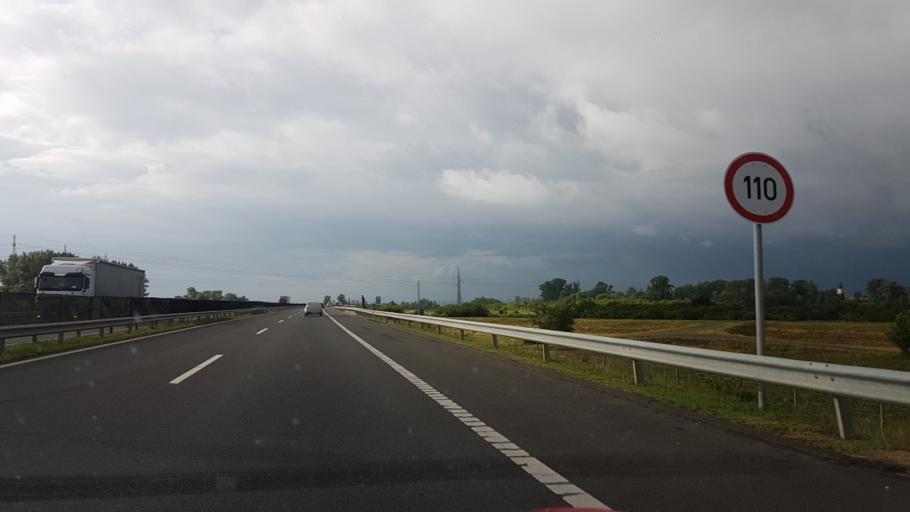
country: HU
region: Borsod-Abauj-Zemplen
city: Felsozsolca
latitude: 48.0935
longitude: 20.8490
